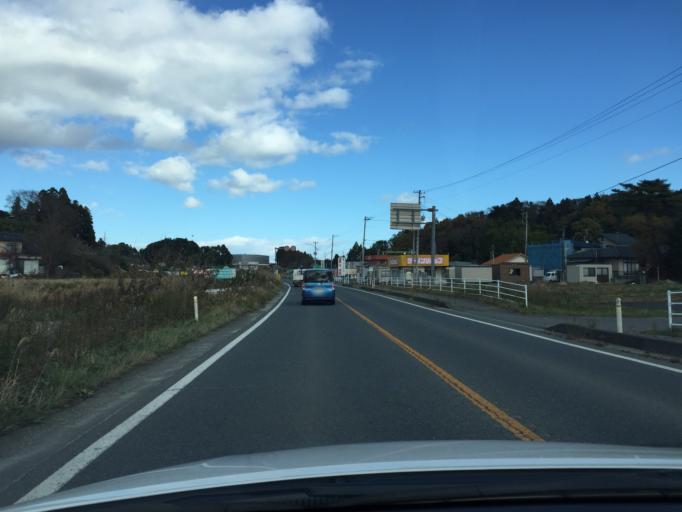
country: JP
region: Fukushima
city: Namie
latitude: 37.6050
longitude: 141.0064
